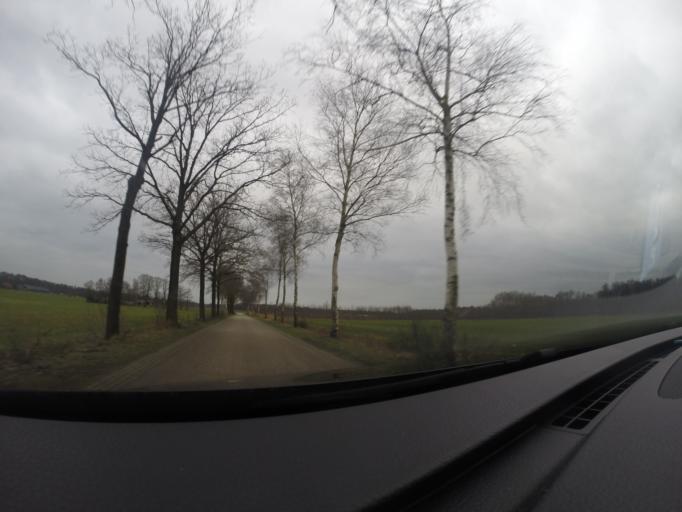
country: NL
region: Overijssel
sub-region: Gemeente Haaksbergen
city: Haaksbergen
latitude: 52.1221
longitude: 6.7352
